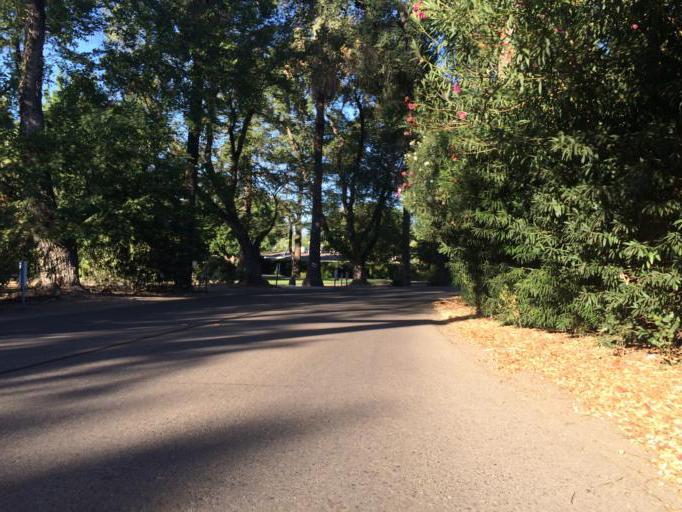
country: US
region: California
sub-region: Fresno County
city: Sunnyside
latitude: 36.7290
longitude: -119.6953
